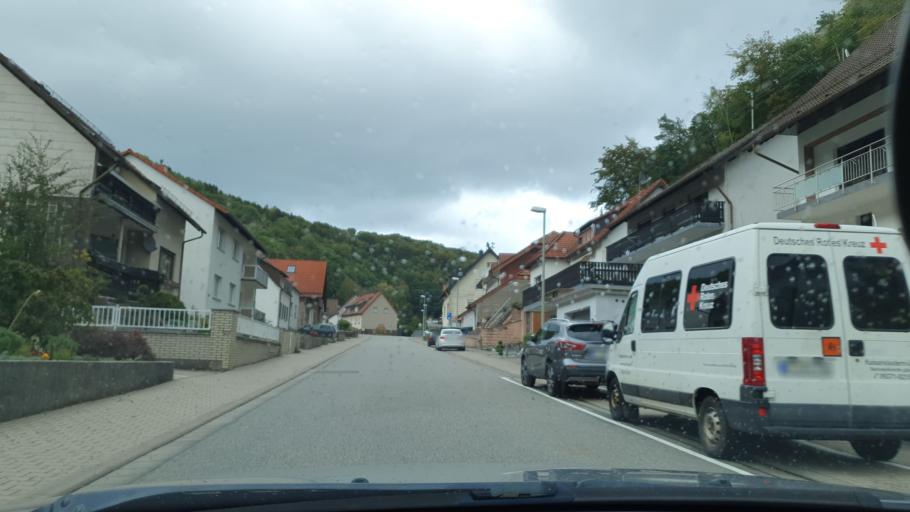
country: DE
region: Rheinland-Pfalz
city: Linden
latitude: 49.3544
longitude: 7.6492
